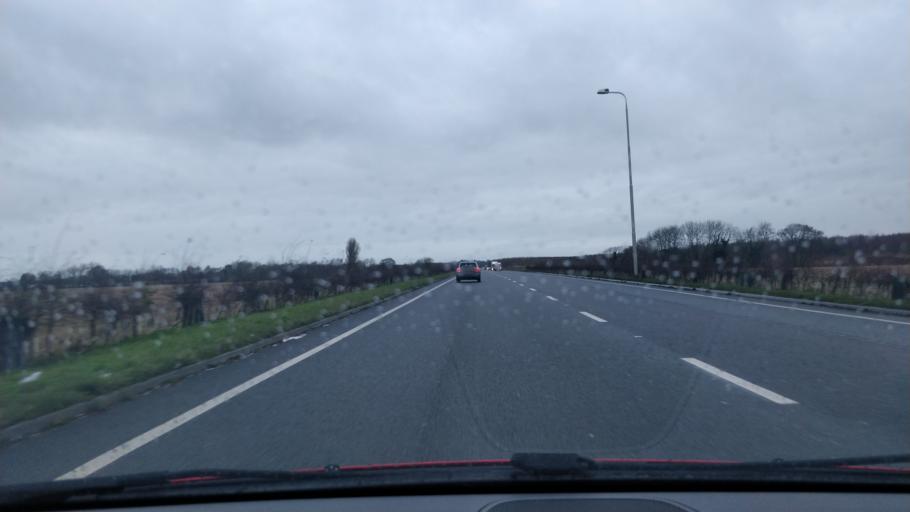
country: GB
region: England
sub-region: Sefton
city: Thornton
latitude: 53.4990
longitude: -2.9839
